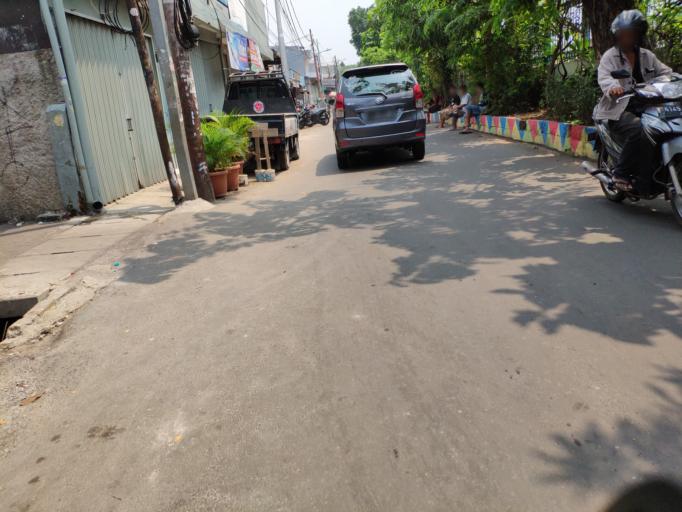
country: ID
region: Jakarta Raya
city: Jakarta
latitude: -6.1966
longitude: 106.8587
